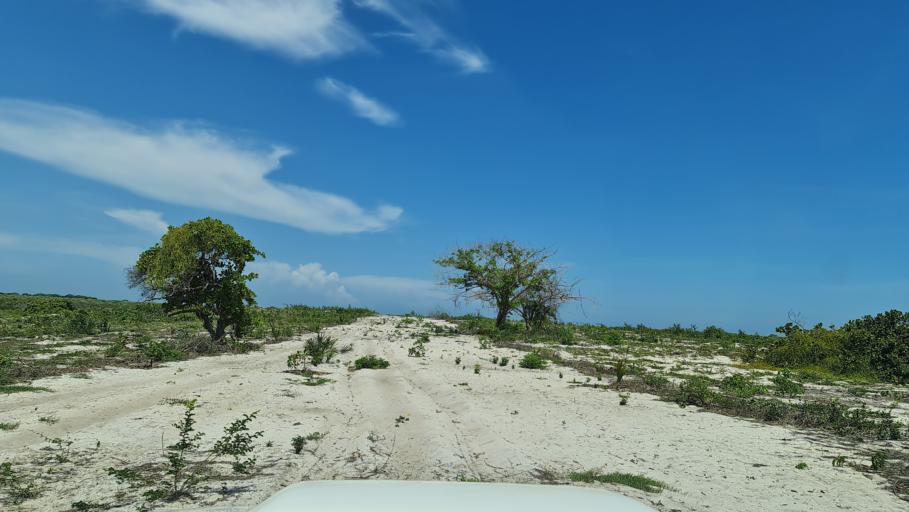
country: MZ
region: Nampula
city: Ilha de Mocambique
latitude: -15.1944
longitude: 40.6221
